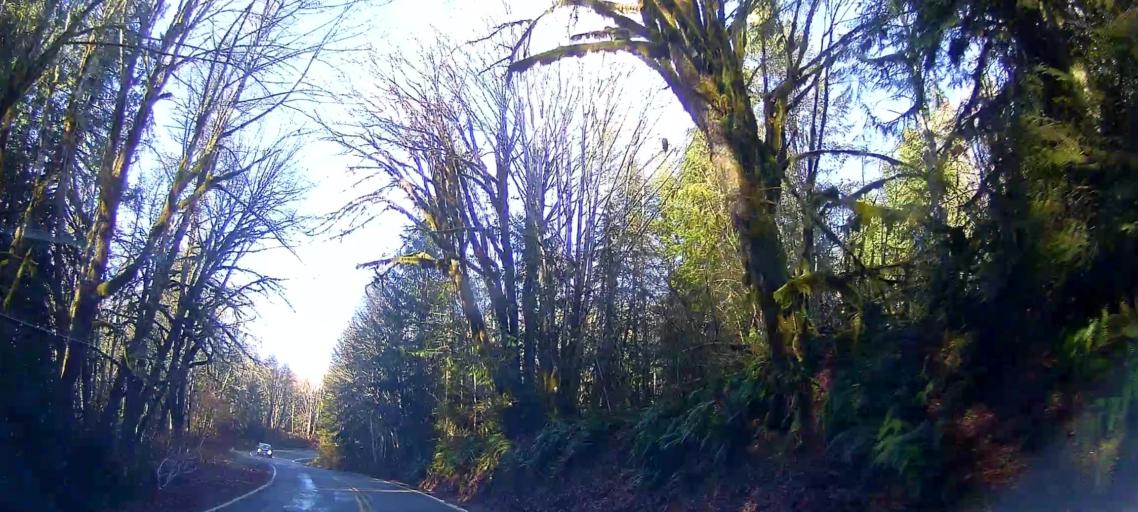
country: US
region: Washington
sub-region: Snohomish County
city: Darrington
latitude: 48.5518
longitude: -121.7665
